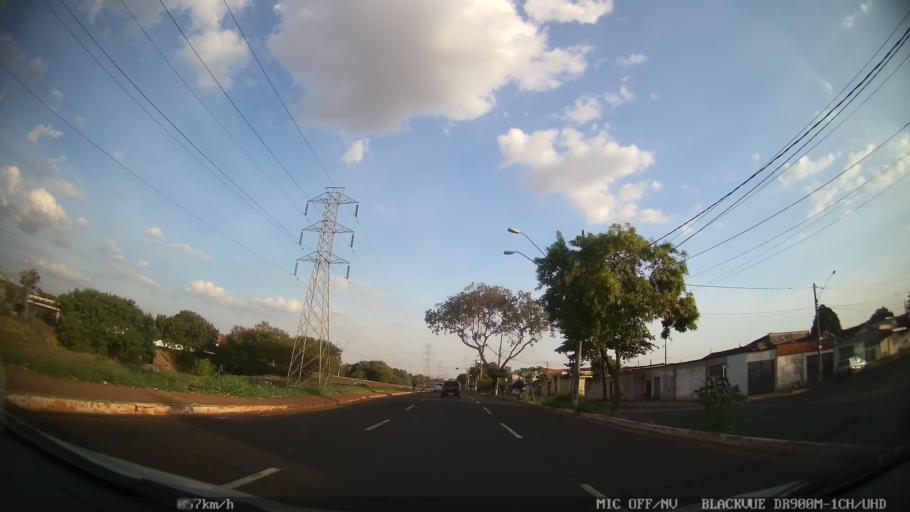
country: BR
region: Sao Paulo
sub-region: Ribeirao Preto
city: Ribeirao Preto
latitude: -21.1265
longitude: -47.8035
